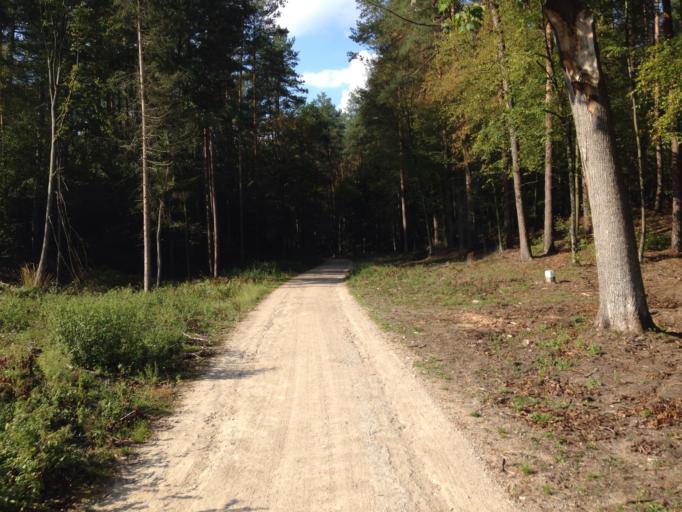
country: PL
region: Kujawsko-Pomorskie
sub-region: Powiat brodnicki
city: Gorzno
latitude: 53.1858
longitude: 19.6721
